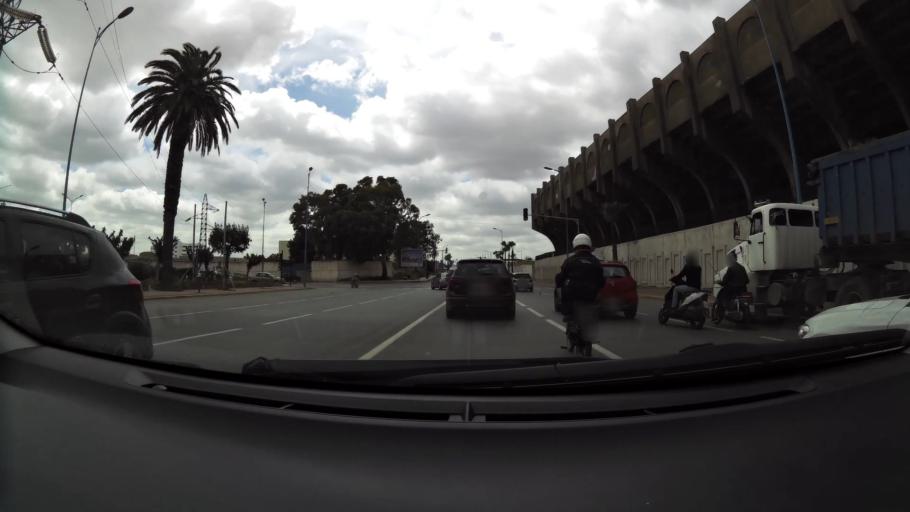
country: MA
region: Grand Casablanca
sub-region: Casablanca
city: Casablanca
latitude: 33.5974
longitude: -7.5454
